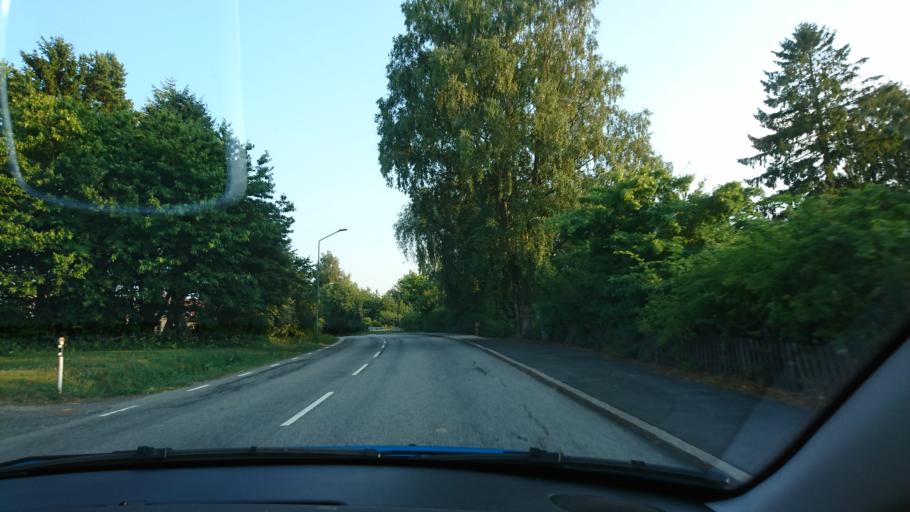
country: SE
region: Skane
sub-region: Simrishamns Kommun
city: Kivik
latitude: 55.6872
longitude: 14.1544
